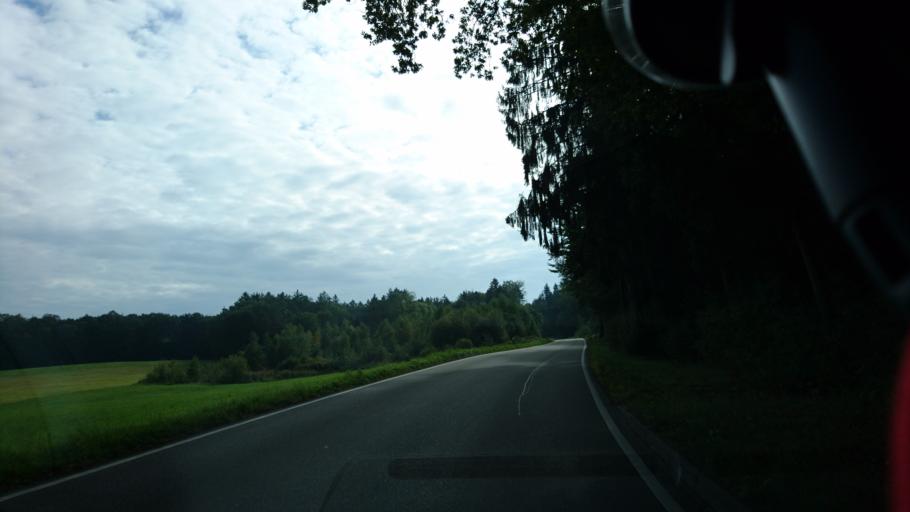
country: DE
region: Baden-Wuerttemberg
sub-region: Regierungsbezirk Stuttgart
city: Mainhardt
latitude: 49.0887
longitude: 9.5894
